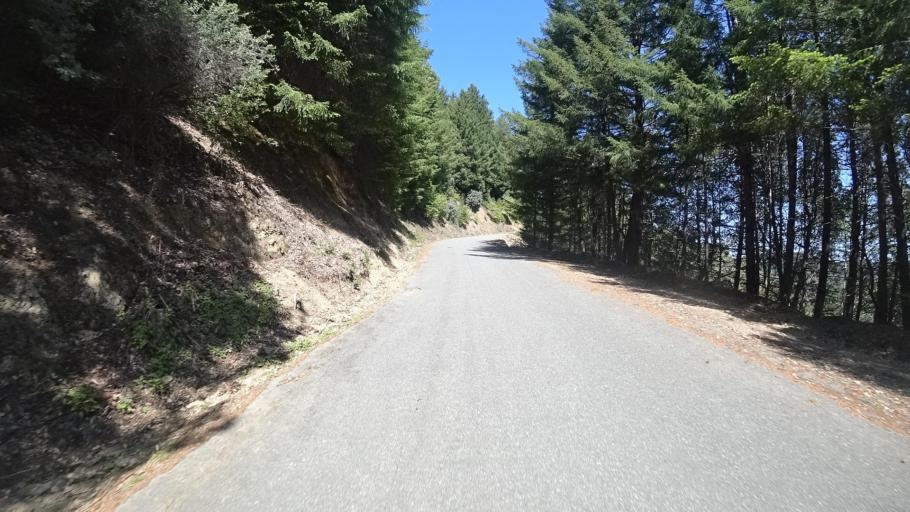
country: US
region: California
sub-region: Humboldt County
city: Redway
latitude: 40.1553
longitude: -124.0710
